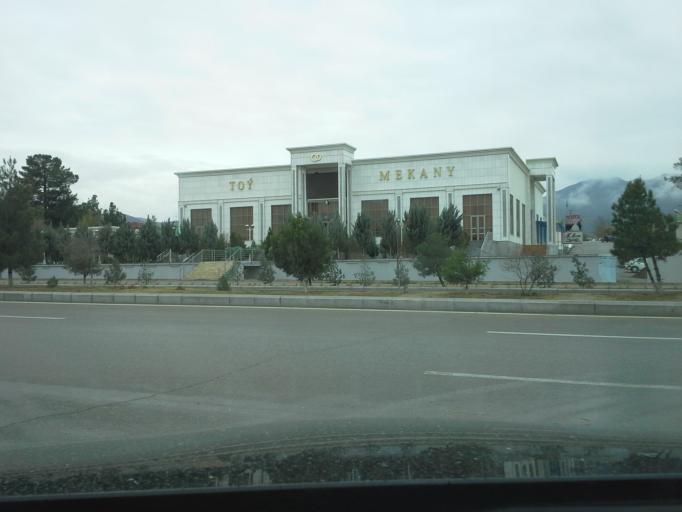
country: TM
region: Ahal
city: Abadan
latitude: 37.9622
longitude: 58.2229
